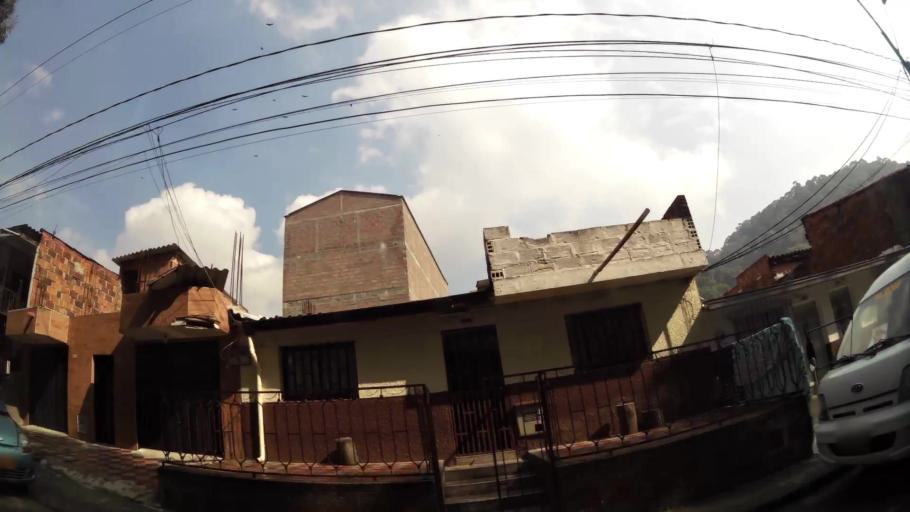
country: CO
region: Antioquia
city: Sabaneta
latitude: 6.1719
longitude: -75.6258
